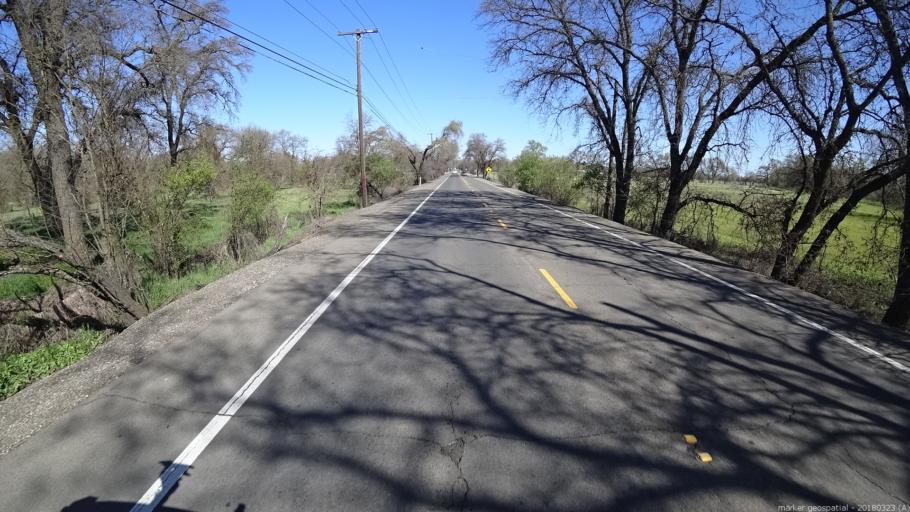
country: US
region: California
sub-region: Sacramento County
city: Rio Linda
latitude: 38.6879
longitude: -121.4384
